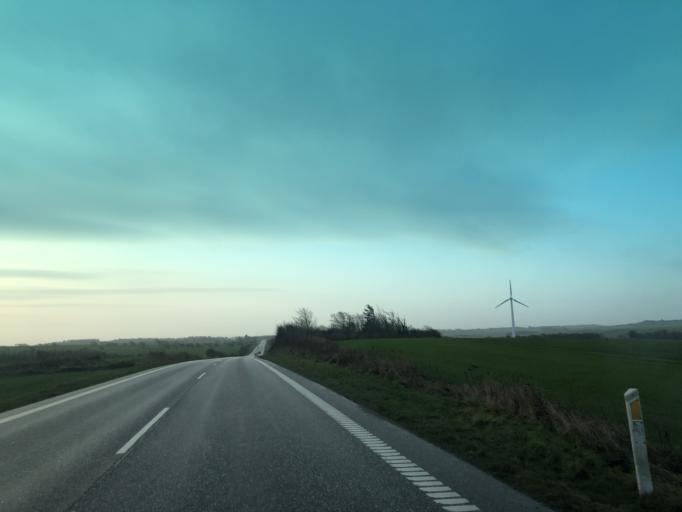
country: DK
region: North Denmark
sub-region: Thisted Kommune
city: Hurup
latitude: 56.7045
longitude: 8.4112
